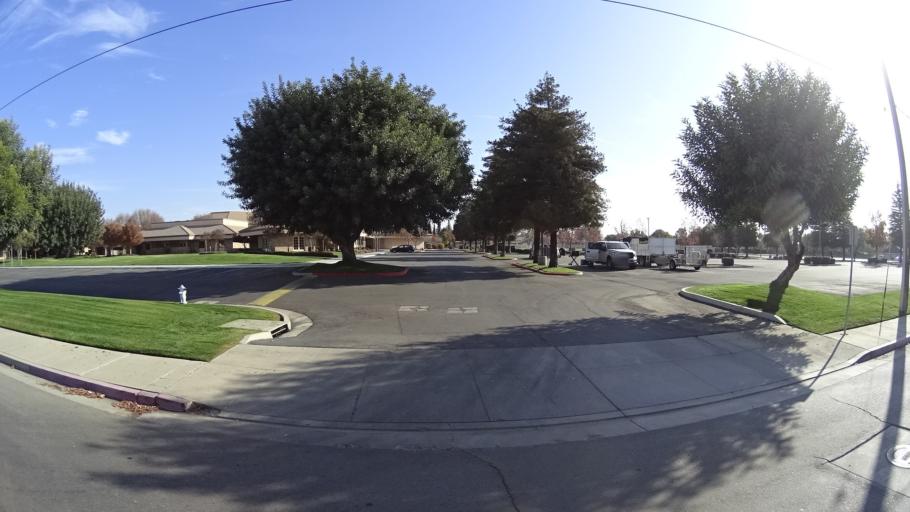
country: US
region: California
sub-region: Kern County
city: Greenacres
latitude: 35.4023
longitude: -119.0743
